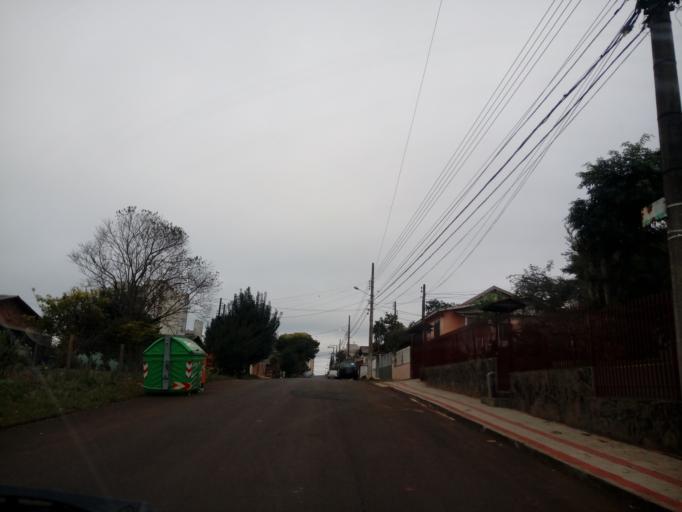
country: BR
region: Santa Catarina
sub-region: Chapeco
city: Chapeco
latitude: -27.0897
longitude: -52.6268
